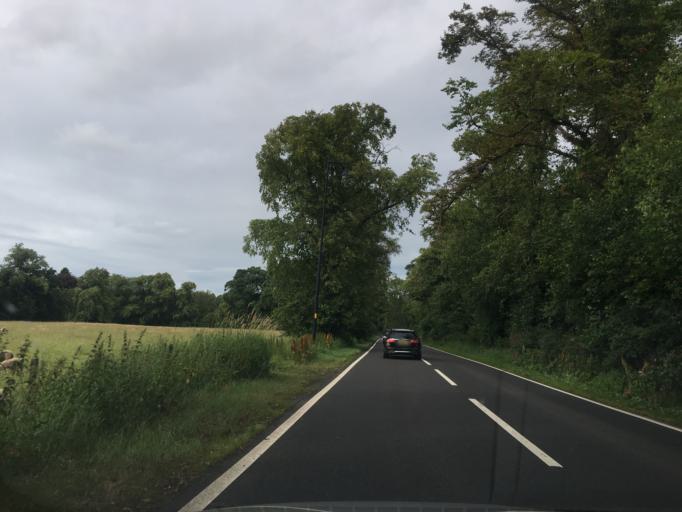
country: GB
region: Scotland
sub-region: South Lanarkshire
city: Biggar
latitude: 55.5606
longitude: -3.6206
